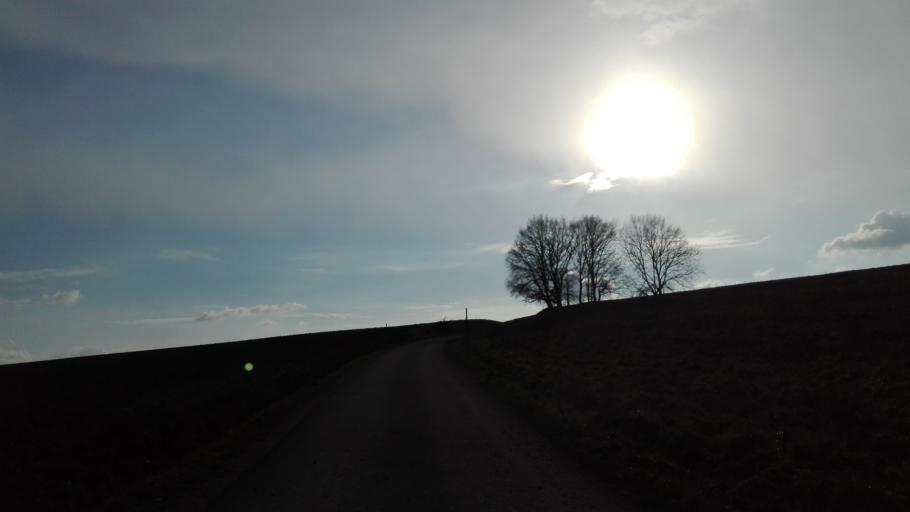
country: AT
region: Upper Austria
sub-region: Politischer Bezirk Perg
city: Perg
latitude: 48.2584
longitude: 14.6110
